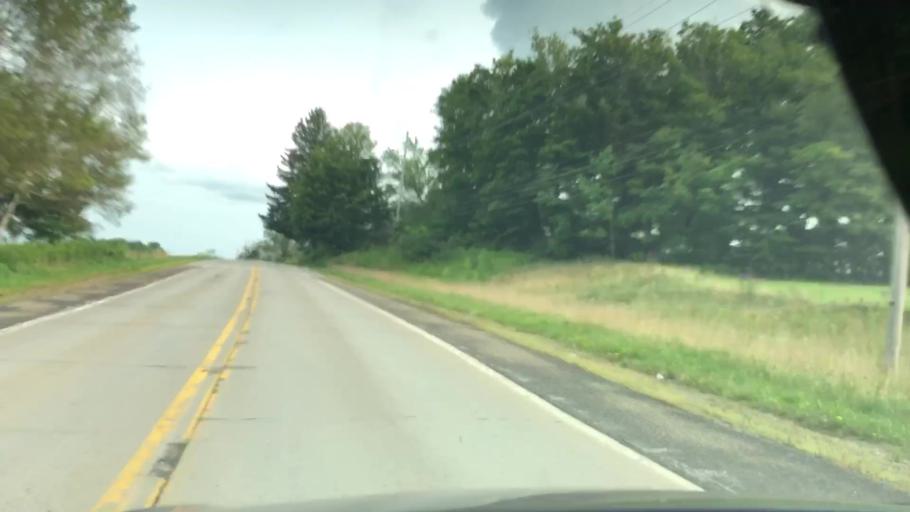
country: US
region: Pennsylvania
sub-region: Erie County
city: Union City
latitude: 41.9569
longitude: -79.8534
